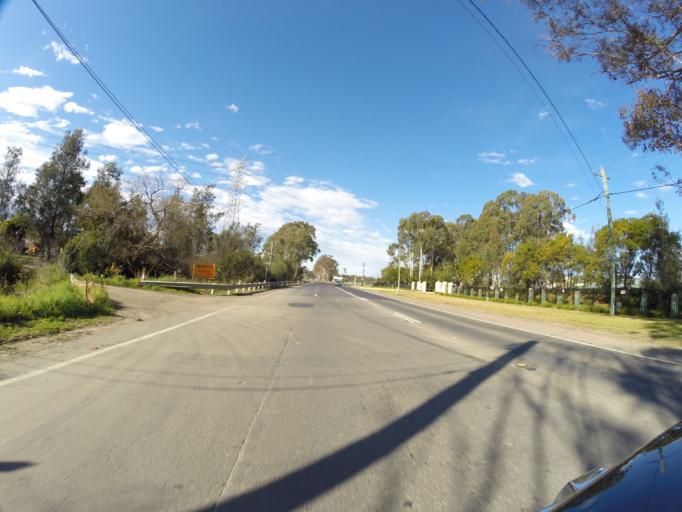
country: AU
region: New South Wales
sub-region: Fairfield
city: Cecil Park
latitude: -33.8808
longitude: 150.8018
